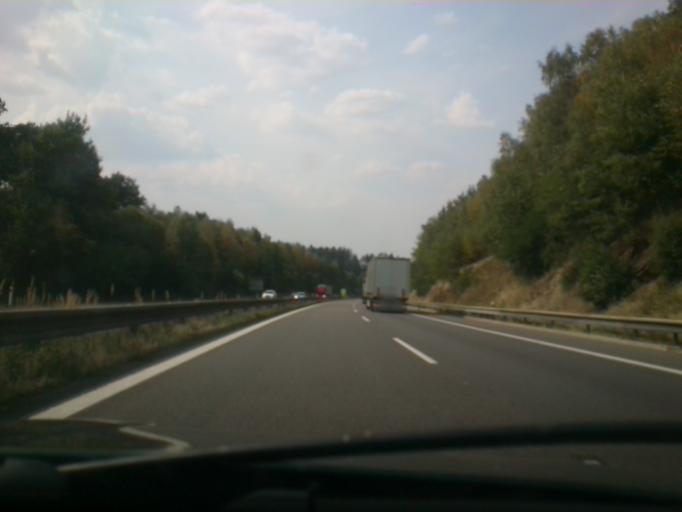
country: CZ
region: Central Bohemia
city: Trhovy Stepanov
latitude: 49.7438
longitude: 15.0332
